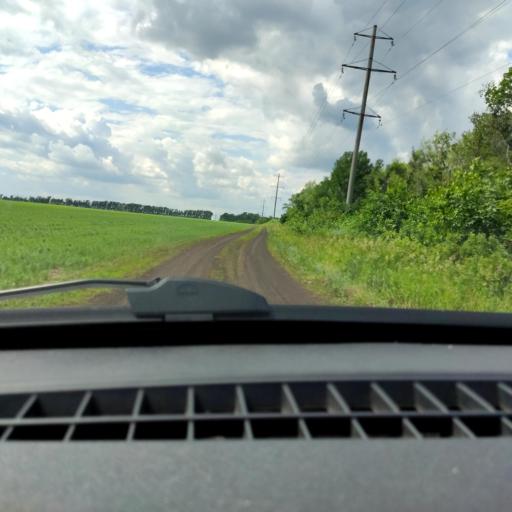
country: RU
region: Bashkortostan
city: Kabakovo
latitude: 54.5145
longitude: 56.0956
